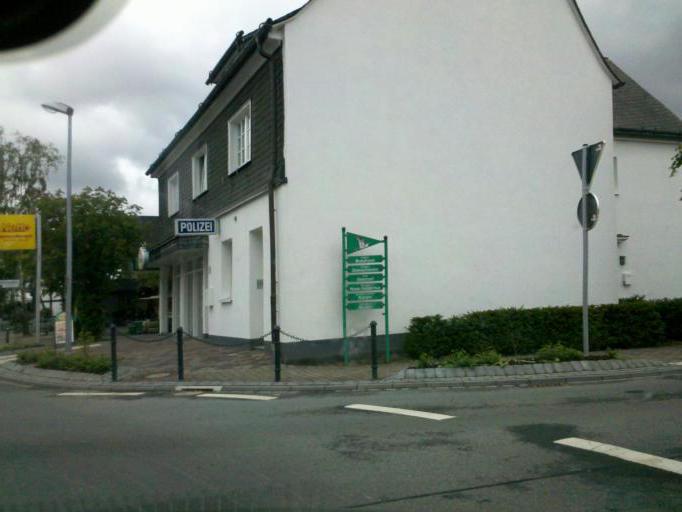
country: DE
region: North Rhine-Westphalia
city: Eslohe
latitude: 51.2543
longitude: 8.1695
